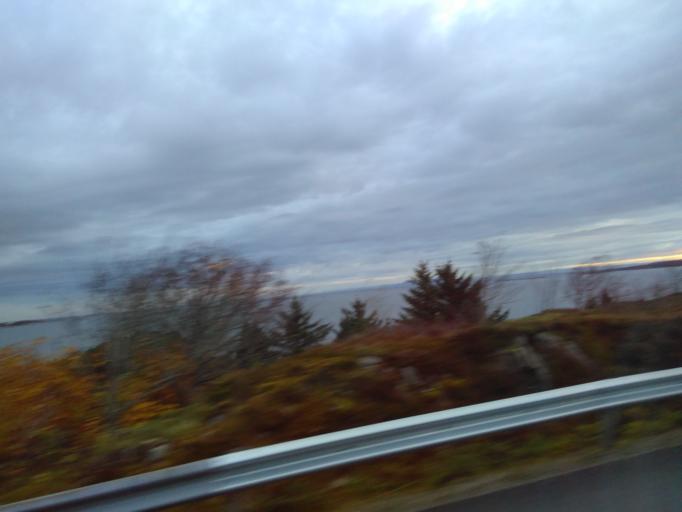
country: NO
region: Sor-Trondelag
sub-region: Froya
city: Sistranda
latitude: 63.7464
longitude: 8.8374
